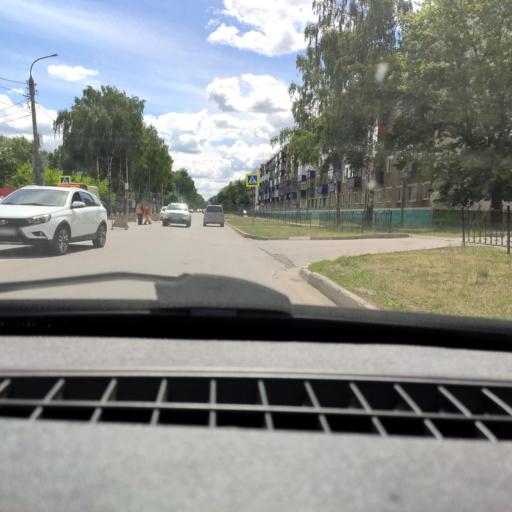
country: RU
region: Bashkortostan
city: Sterlitamak
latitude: 53.6401
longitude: 55.9315
